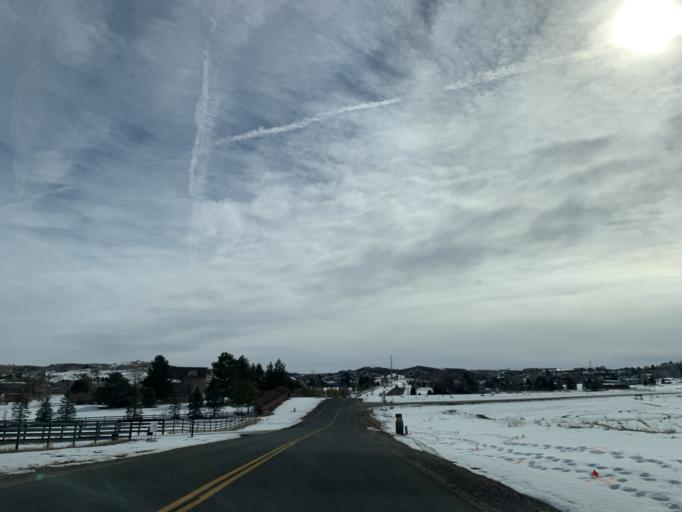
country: US
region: Colorado
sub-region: Douglas County
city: Carriage Club
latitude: 39.5186
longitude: -104.9104
